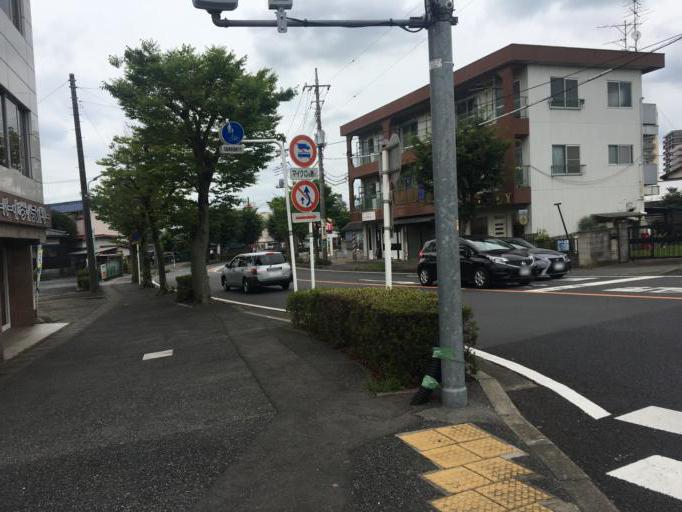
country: JP
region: Saitama
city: Kasukabe
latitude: 35.9784
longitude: 139.7633
